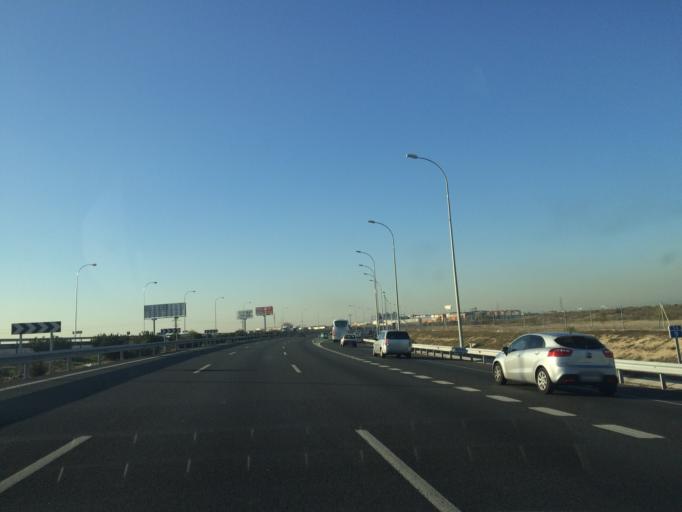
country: ES
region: Madrid
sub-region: Provincia de Madrid
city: Alcorcon
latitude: 40.3843
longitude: -3.8226
